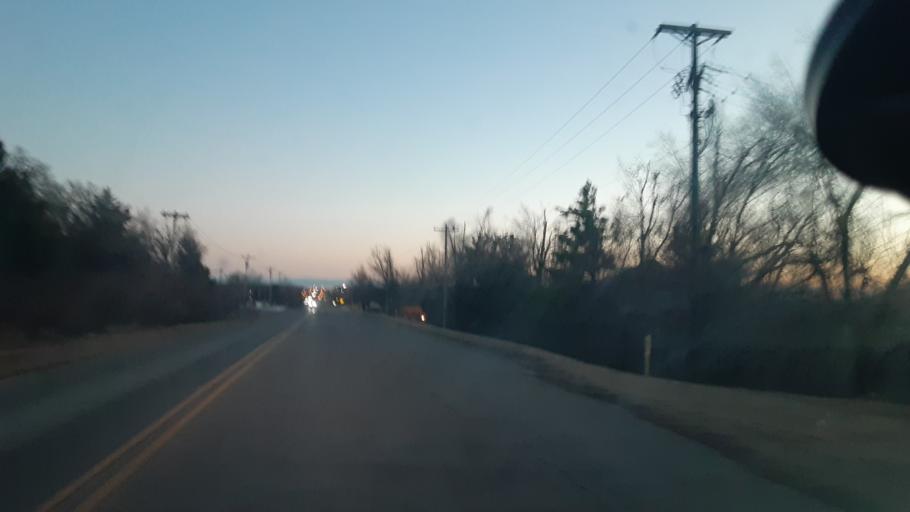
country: US
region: Oklahoma
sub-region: Oklahoma County
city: Edmond
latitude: 35.6576
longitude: -97.4247
